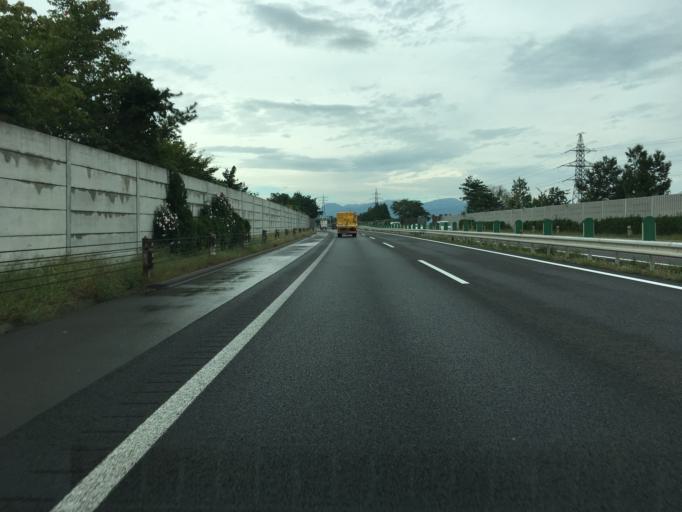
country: JP
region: Fukushima
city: Fukushima-shi
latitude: 37.7667
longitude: 140.4116
